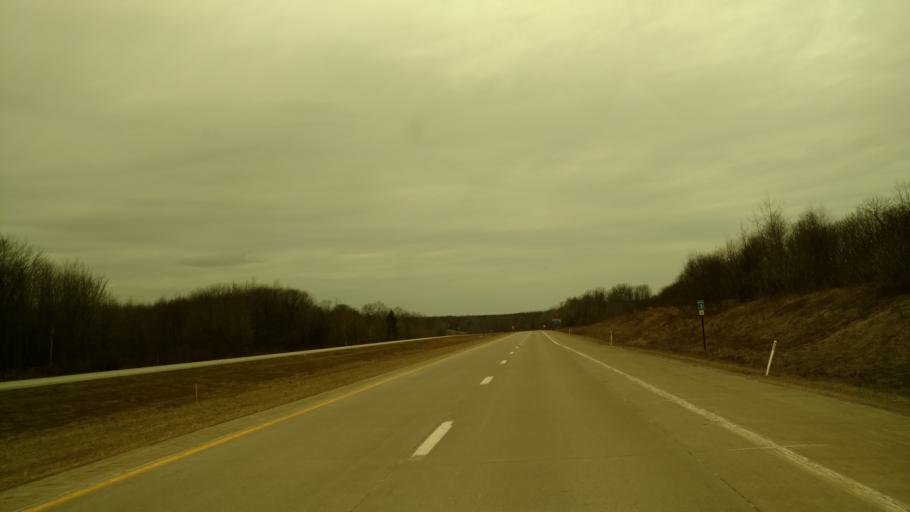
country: US
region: Pennsylvania
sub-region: Erie County
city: North East
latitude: 42.1422
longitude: -79.8299
